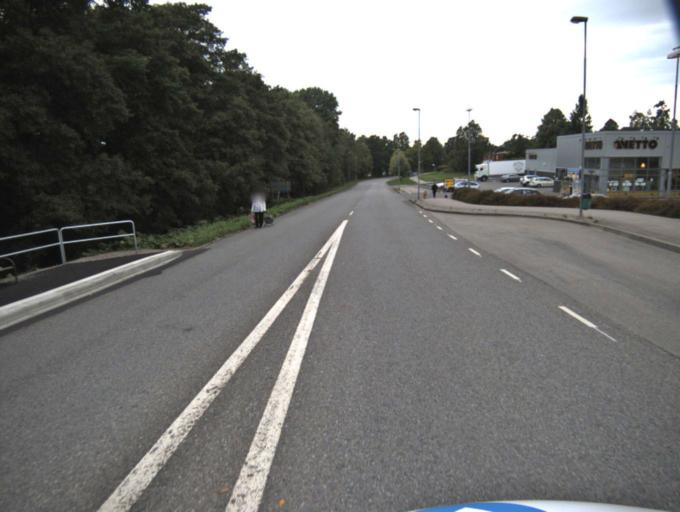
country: SE
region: Vaestra Goetaland
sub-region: Ulricehamns Kommun
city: Ulricehamn
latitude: 57.7797
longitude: 13.4141
